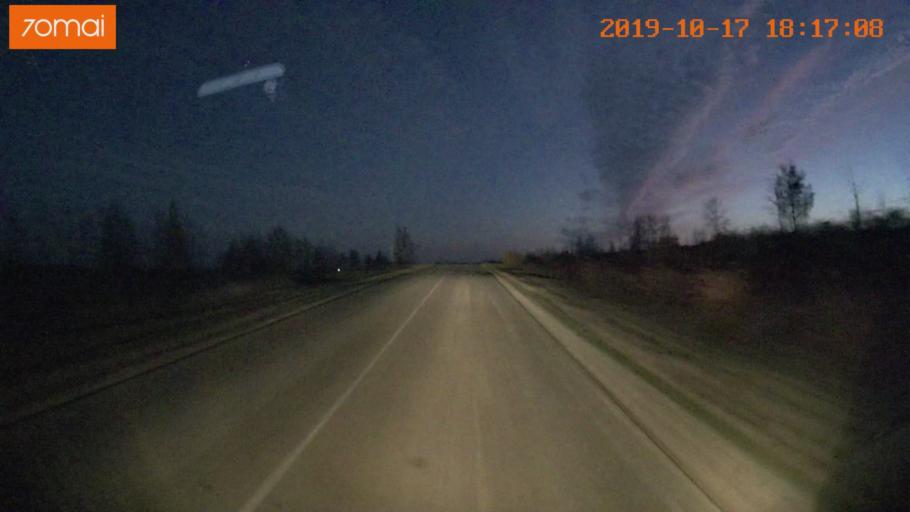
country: RU
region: Tula
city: Kurkino
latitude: 53.3931
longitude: 38.5068
